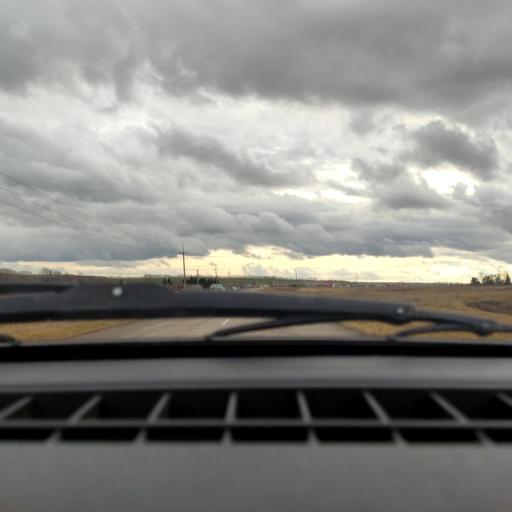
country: RU
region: Bashkortostan
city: Asanovo
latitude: 54.9314
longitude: 55.5183
